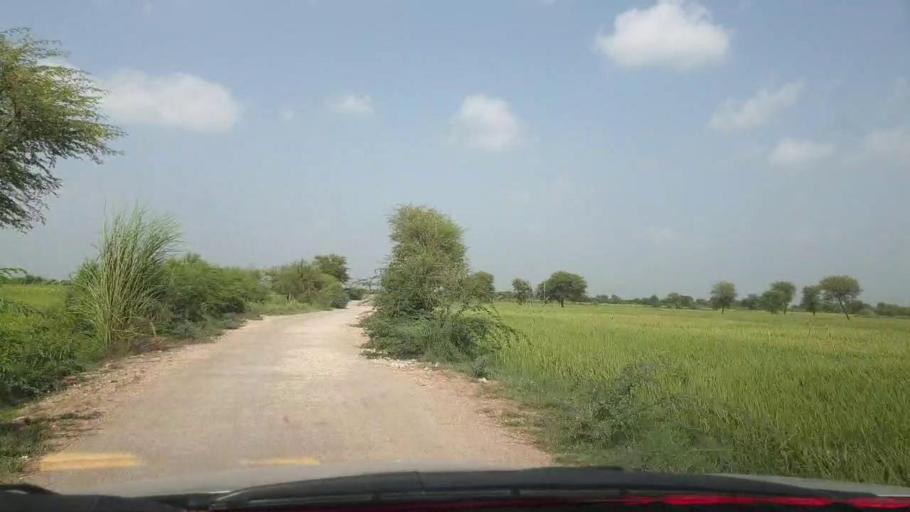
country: PK
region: Sindh
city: Tando Bago
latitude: 24.8670
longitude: 68.9251
